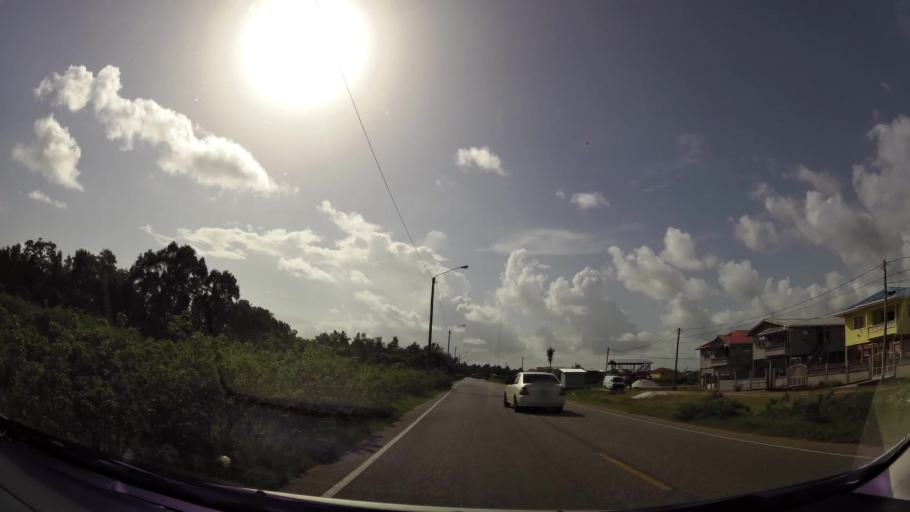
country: GY
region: Demerara-Mahaica
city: Mahaica Village
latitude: 6.7376
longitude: -57.9510
